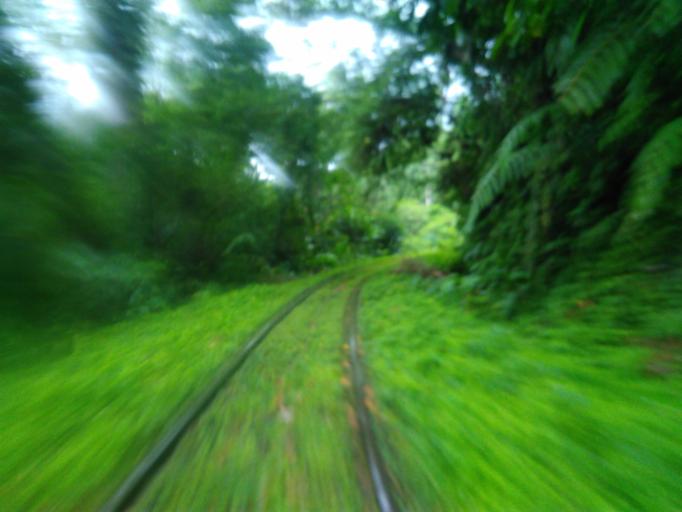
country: CO
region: Valle del Cauca
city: Buenaventura
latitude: 3.8453
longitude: -76.8822
